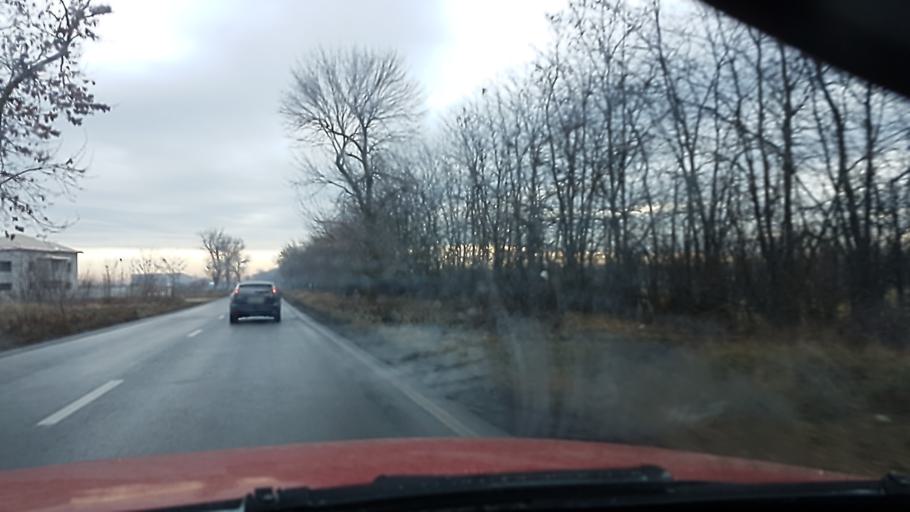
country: RO
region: Calarasi
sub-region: Comuna Frumusani
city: Frumusani
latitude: 44.3215
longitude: 26.2677
